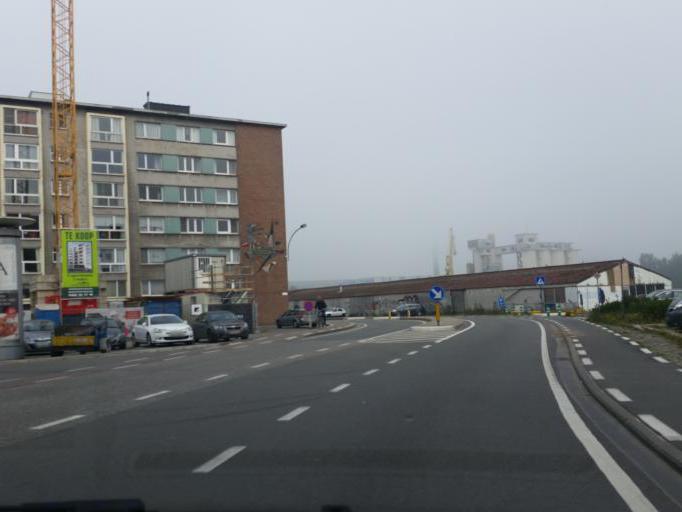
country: BE
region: Flanders
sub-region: Provincie Oost-Vlaanderen
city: Gent
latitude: 51.0643
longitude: 3.7342
